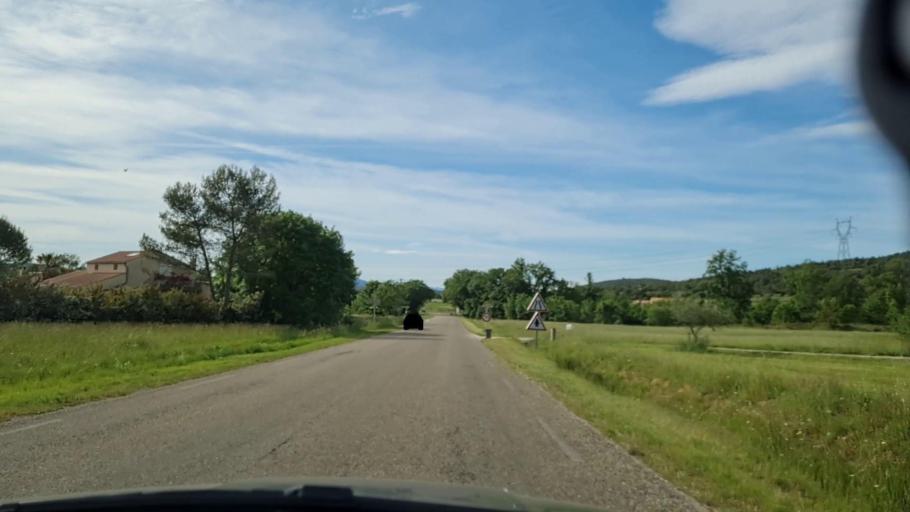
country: FR
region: Languedoc-Roussillon
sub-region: Departement du Gard
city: Villevieille
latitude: 43.8327
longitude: 4.0884
